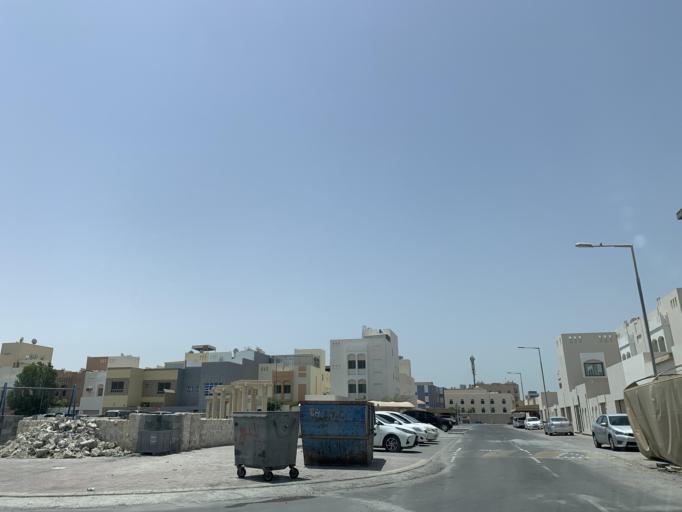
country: BH
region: Northern
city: Sitrah
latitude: 26.1400
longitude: 50.5904
